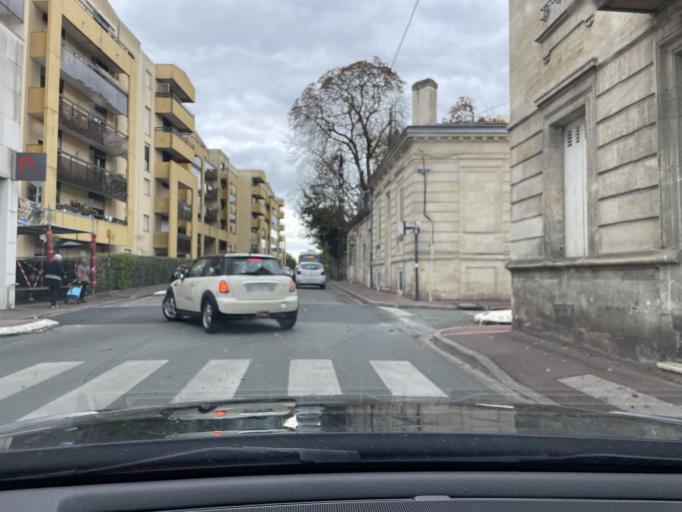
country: FR
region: Aquitaine
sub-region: Departement de la Gironde
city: Le Bouscat
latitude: 44.8613
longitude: -0.5898
